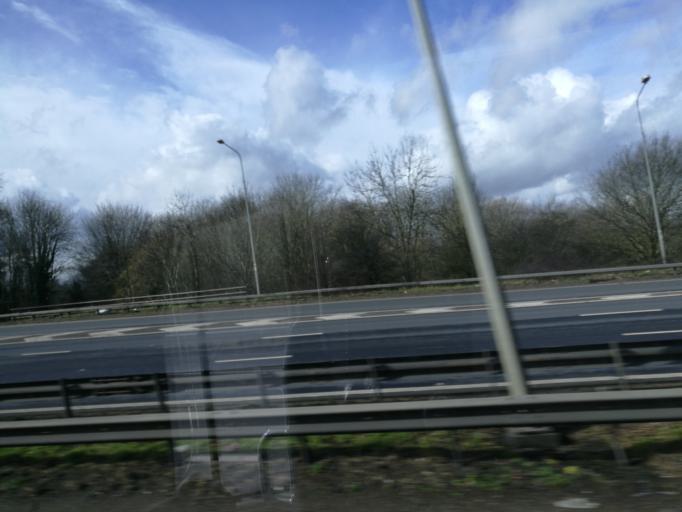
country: GB
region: England
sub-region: Hertfordshire
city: Watford
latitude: 51.6751
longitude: -0.3726
